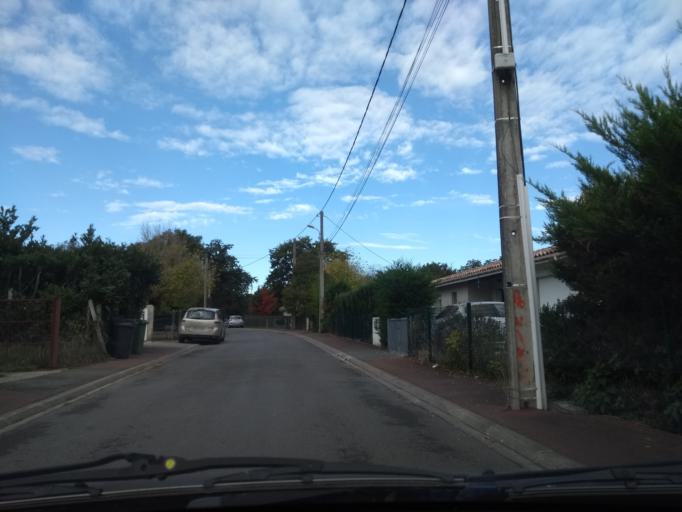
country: FR
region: Aquitaine
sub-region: Departement de la Gironde
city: Gradignan
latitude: 44.7800
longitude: -0.6145
